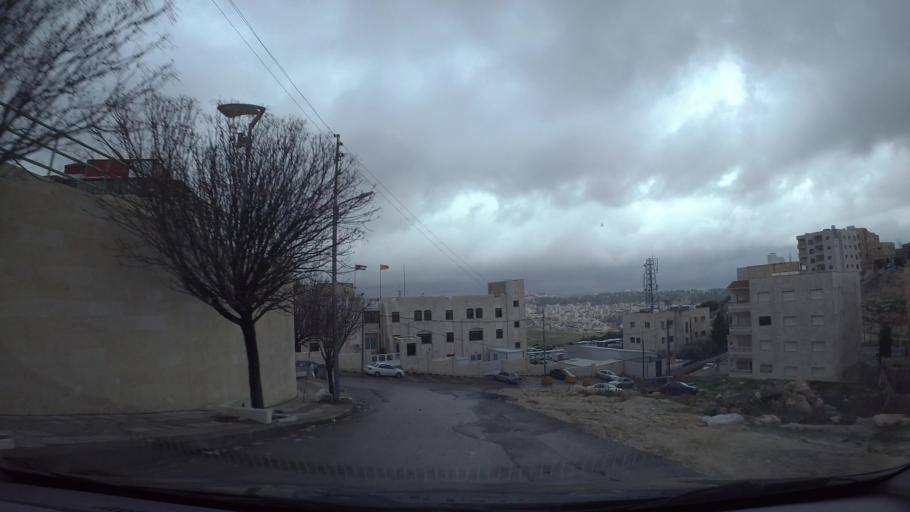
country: JO
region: Amman
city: Amman
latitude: 32.0085
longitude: 35.9326
